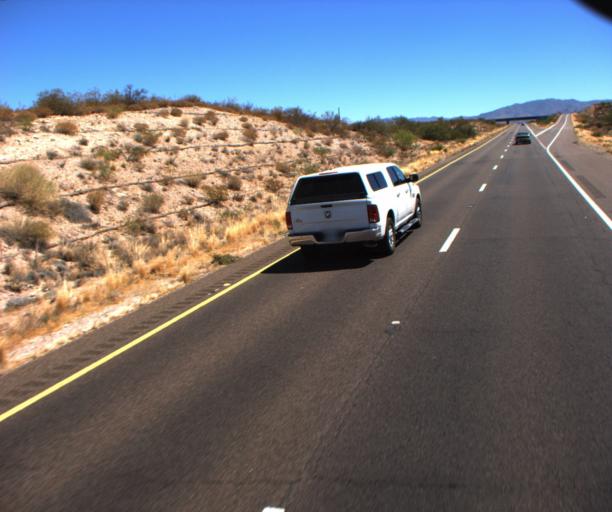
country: US
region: Arizona
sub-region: Maricopa County
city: Rio Verde
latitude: 33.6230
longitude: -111.5645
